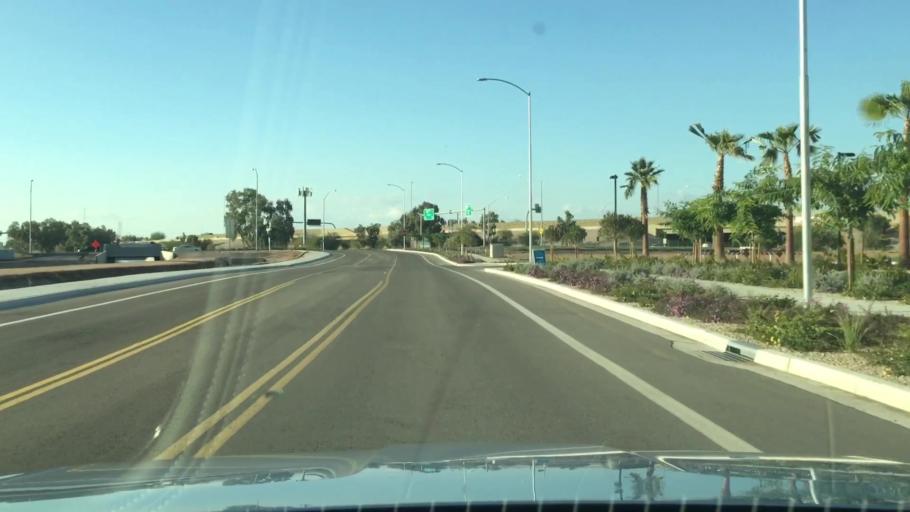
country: US
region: Arizona
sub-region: Maricopa County
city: Gilbert
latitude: 33.3839
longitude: -111.7357
